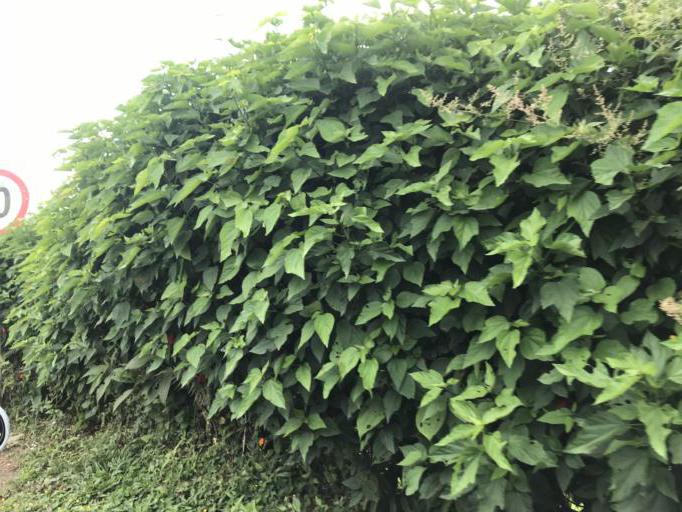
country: CO
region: Valle del Cauca
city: Cali
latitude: 3.5182
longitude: -76.6055
